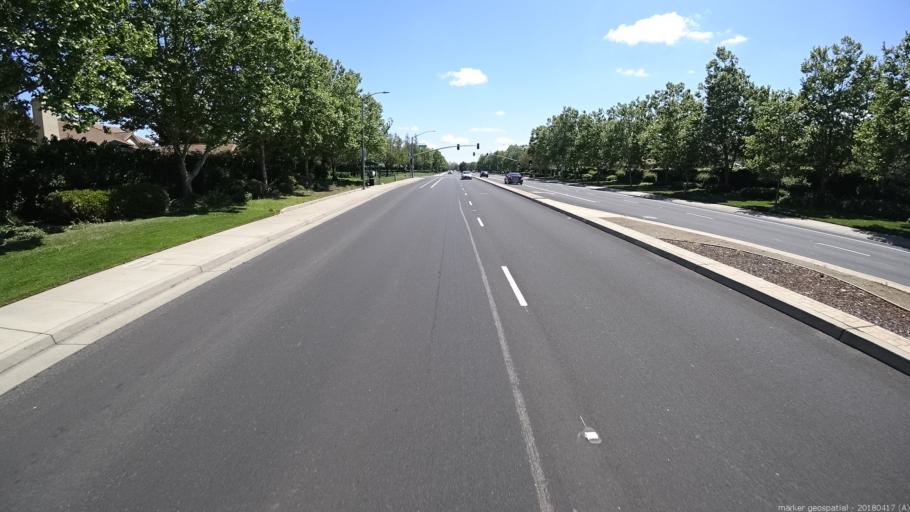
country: US
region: California
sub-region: Sacramento County
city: Laguna
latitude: 38.4184
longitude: -121.4810
